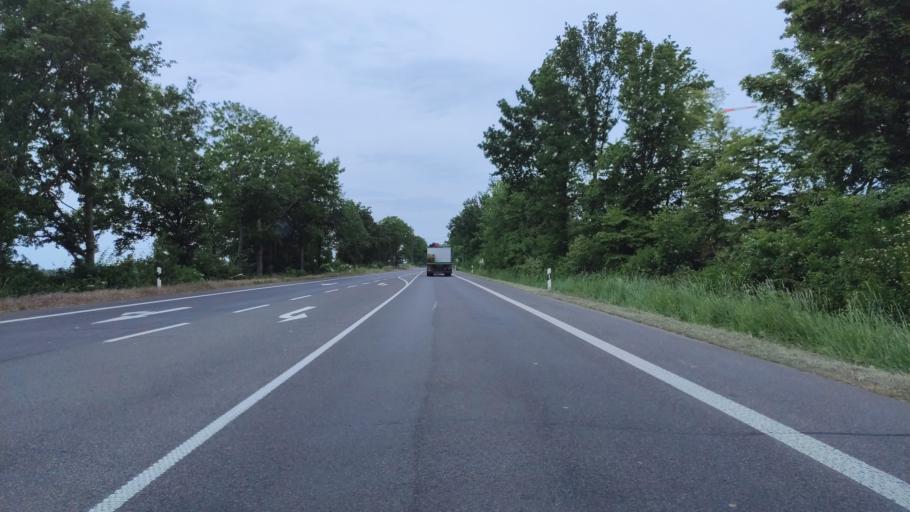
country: DE
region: North Rhine-Westphalia
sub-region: Regierungsbezirk Dusseldorf
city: Kaarst
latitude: 51.1762
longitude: 6.5882
